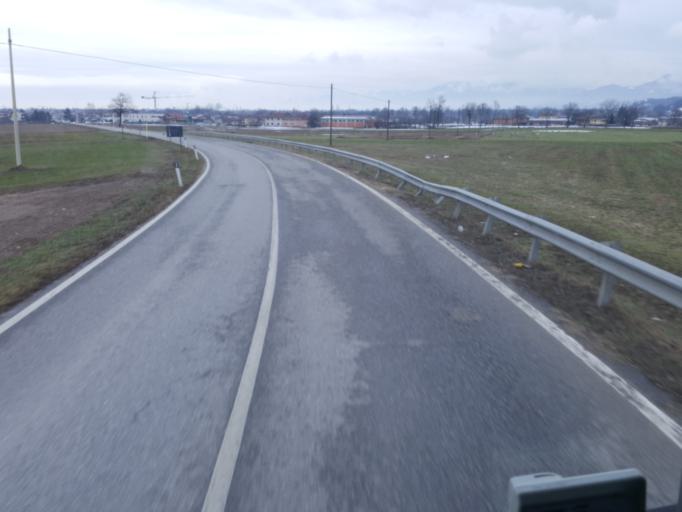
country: IT
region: Piedmont
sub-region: Provincia di Cuneo
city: Bernezzo
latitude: 44.4010
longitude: 7.4488
